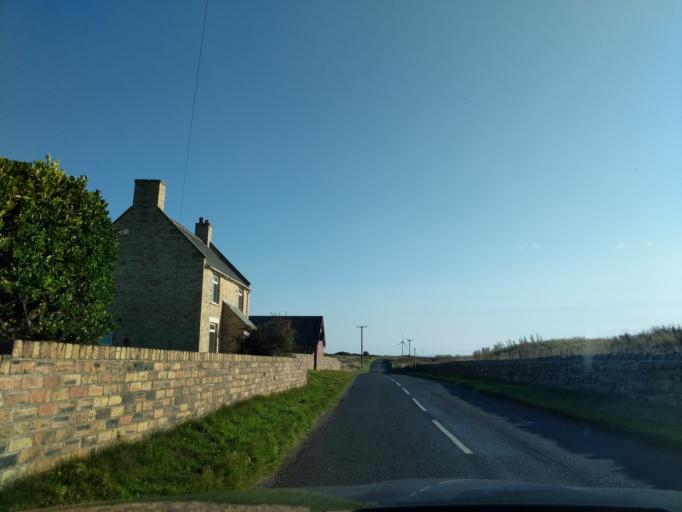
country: GB
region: England
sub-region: Northumberland
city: Lynemouth
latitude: 55.2280
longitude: -1.5291
